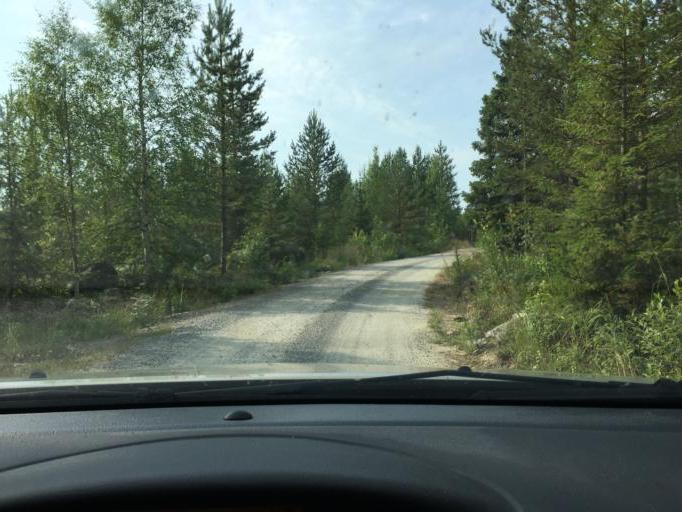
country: SE
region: Norrbotten
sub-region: Kalix Kommun
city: Rolfs
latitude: 65.7648
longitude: 23.0021
